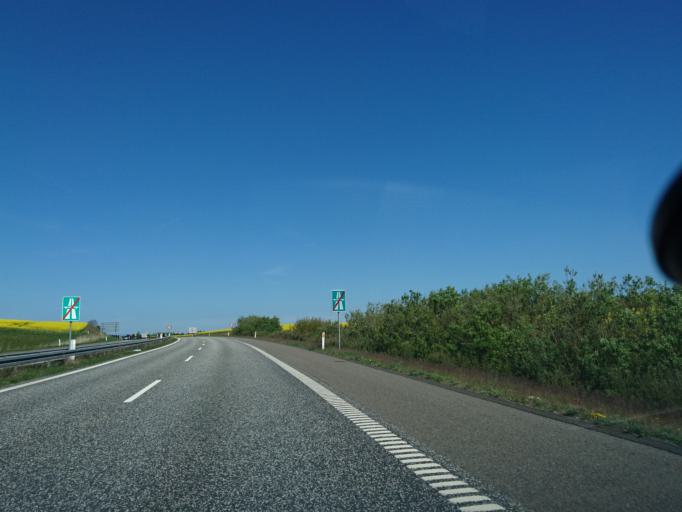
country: DK
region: North Denmark
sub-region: Hjorring Kommune
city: Hirtshals
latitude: 57.5602
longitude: 10.0153
